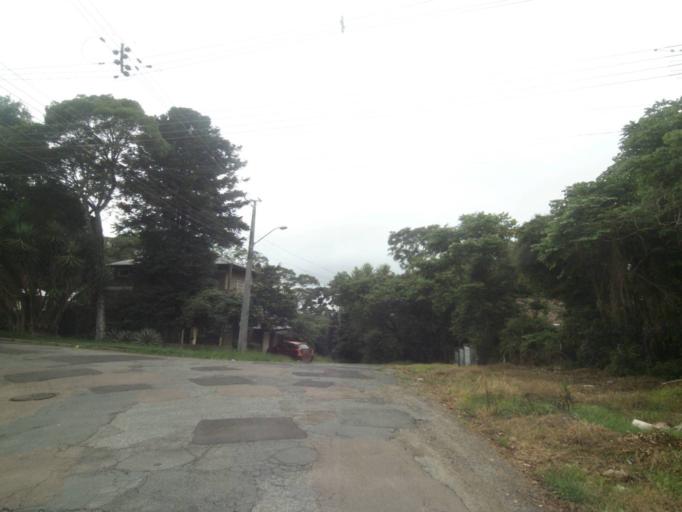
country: BR
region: Parana
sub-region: Curitiba
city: Curitiba
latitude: -25.3963
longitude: -49.2795
